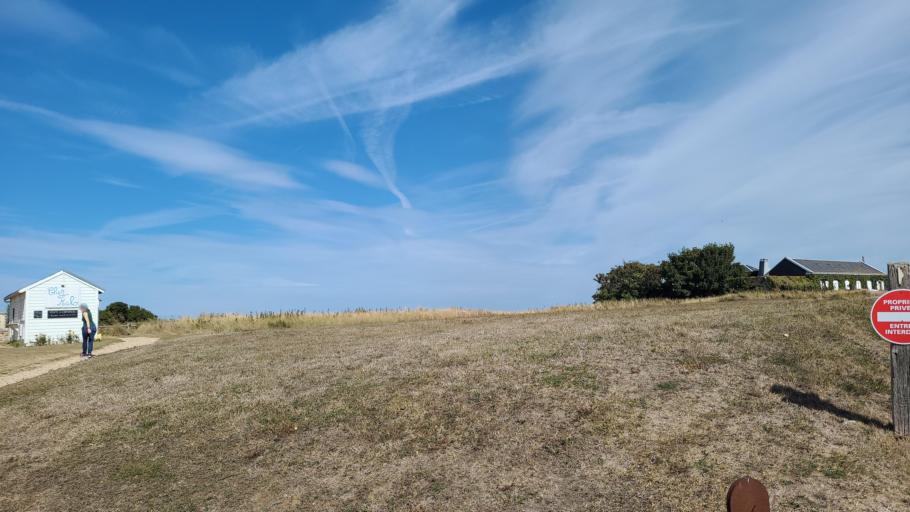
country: FR
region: Haute-Normandie
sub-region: Departement de la Seine-Maritime
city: Fecamp
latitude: 49.7670
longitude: 0.3705
